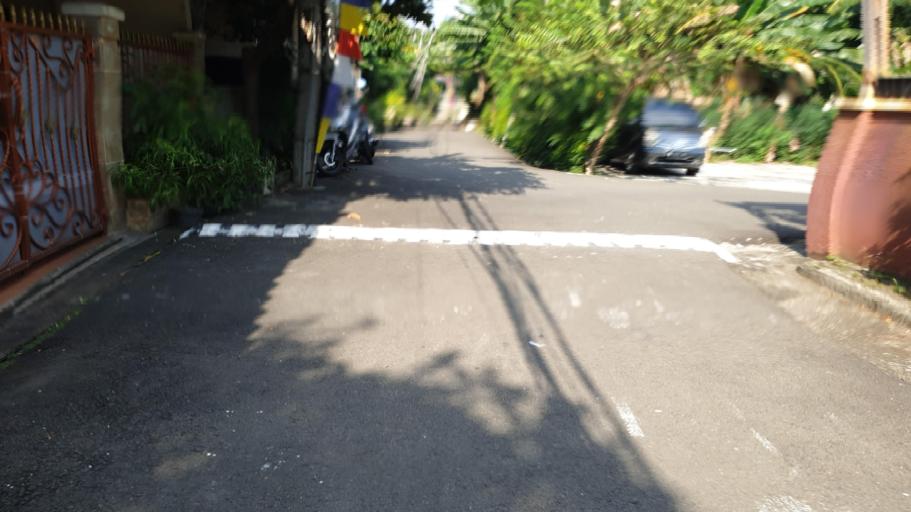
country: ID
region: Jakarta Raya
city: Jakarta
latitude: -6.2987
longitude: 106.8380
